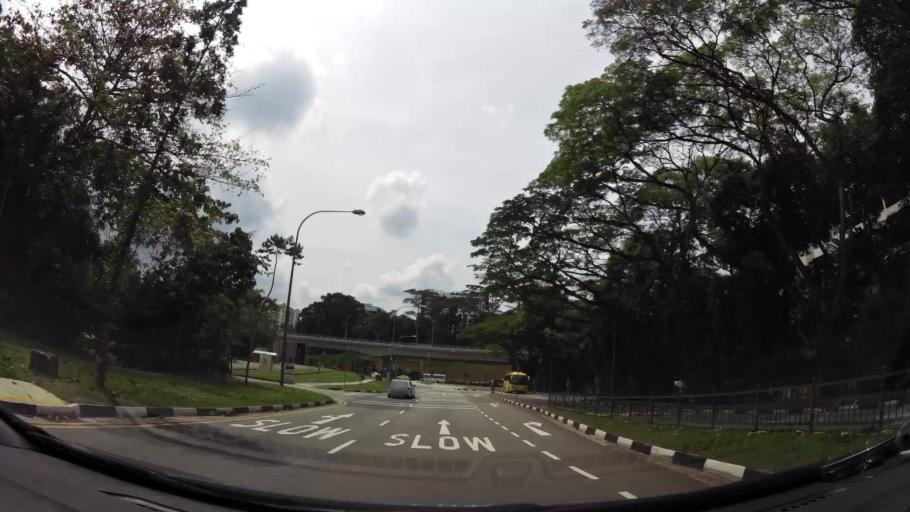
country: MY
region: Johor
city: Johor Bahru
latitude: 1.3636
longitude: 103.7689
